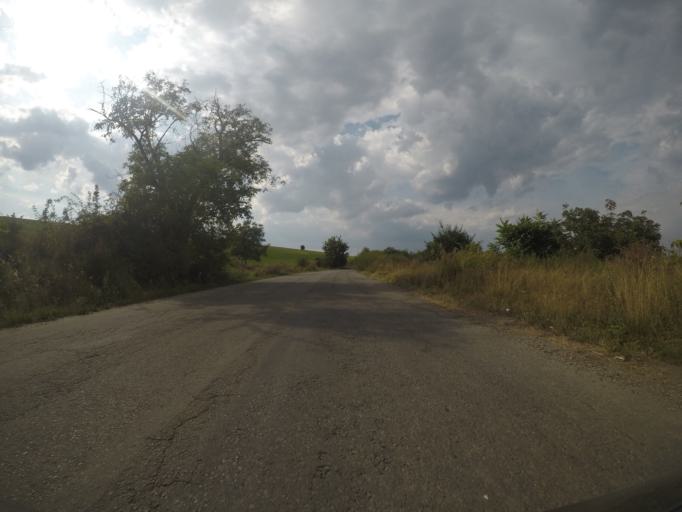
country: RO
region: Cluj
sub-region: Comuna Sandulesti
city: Copaceni
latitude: 46.5821
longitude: 23.7573
